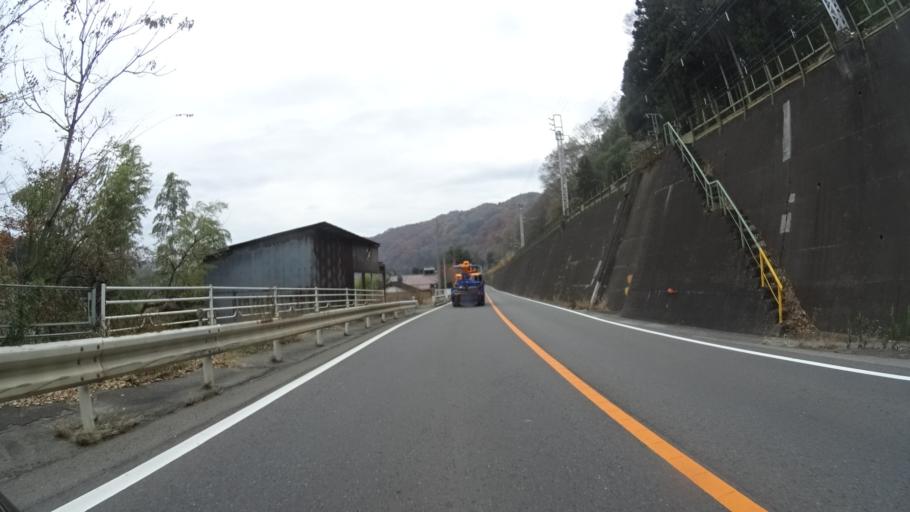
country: JP
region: Gunma
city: Numata
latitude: 36.6156
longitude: 139.0421
